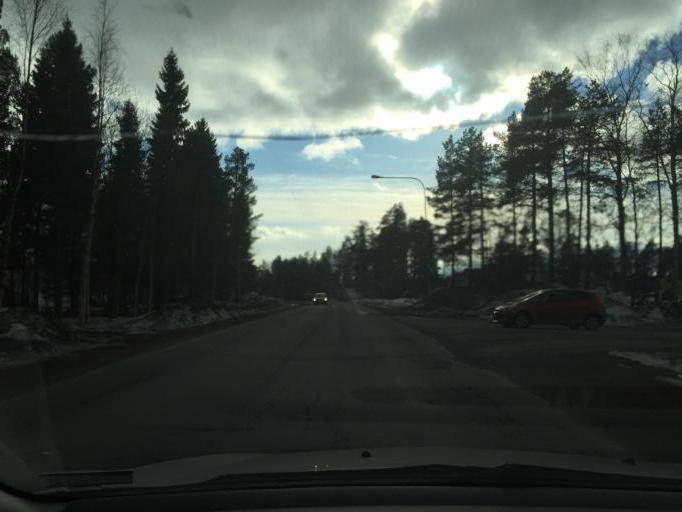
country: SE
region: Norrbotten
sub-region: Lulea Kommun
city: Lulea
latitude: 65.5934
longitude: 22.2295
